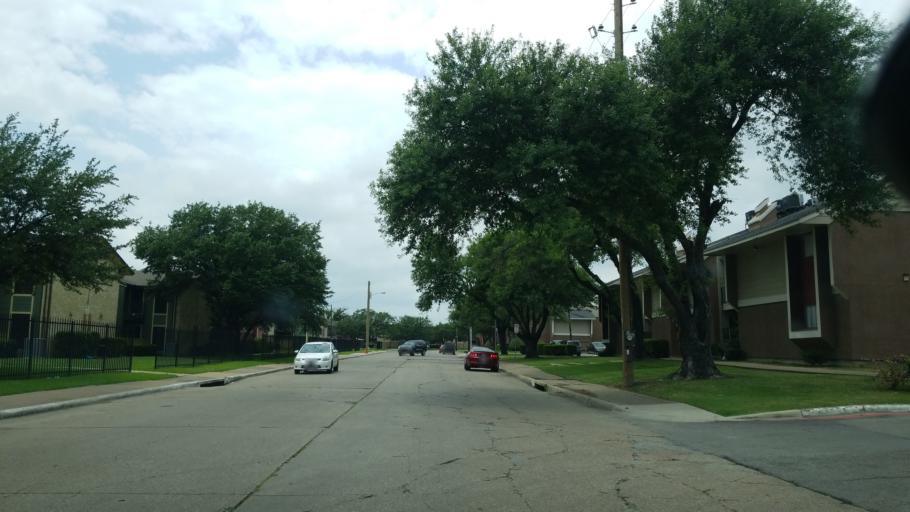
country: US
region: Texas
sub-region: Dallas County
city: Farmers Branch
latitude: 32.8745
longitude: -96.8680
